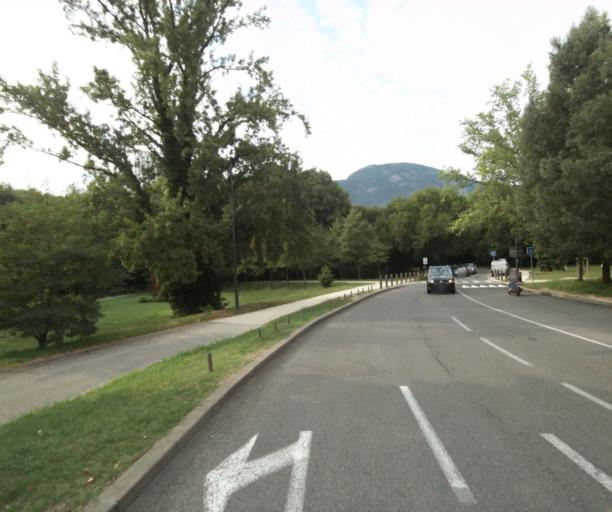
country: FR
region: Rhone-Alpes
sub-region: Departement de l'Isere
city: La Tronche
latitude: 45.1899
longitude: 5.7413
